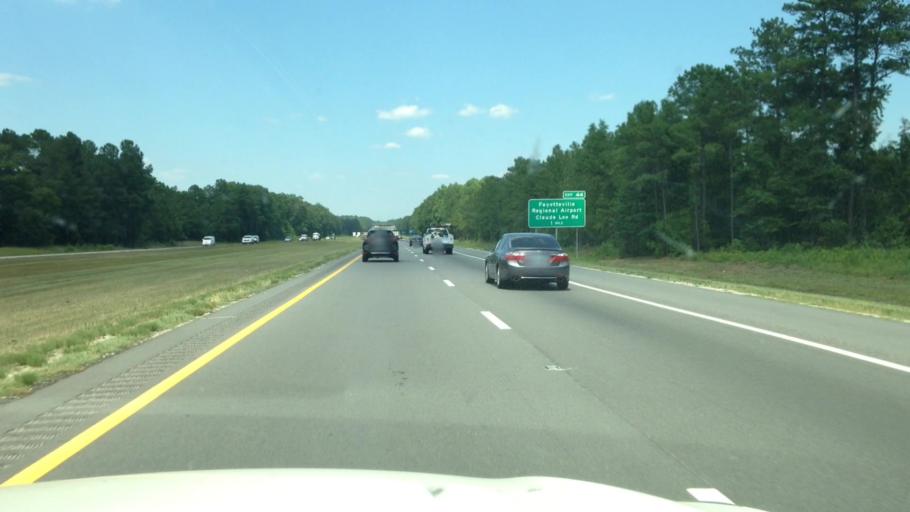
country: US
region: North Carolina
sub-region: Cumberland County
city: Hope Mills
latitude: 34.9481
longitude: -78.9051
